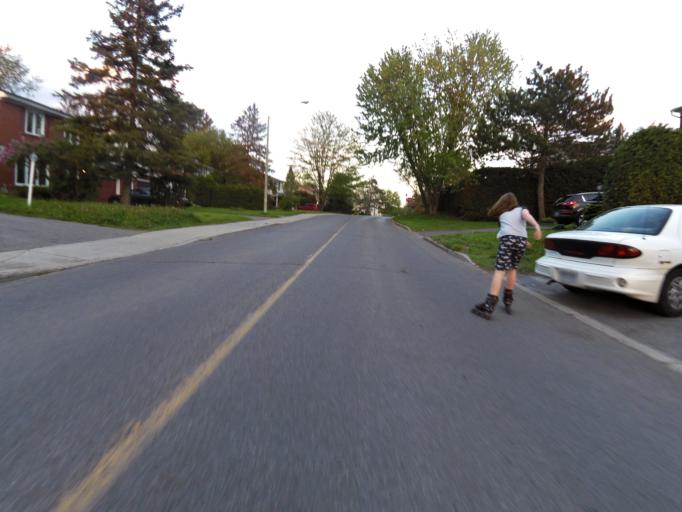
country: CA
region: Ontario
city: Bells Corners
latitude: 45.3268
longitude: -75.7896
